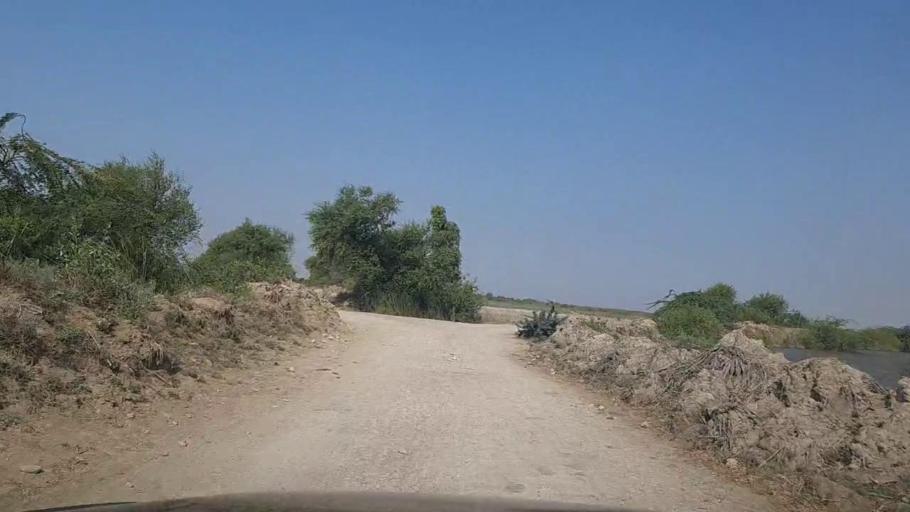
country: PK
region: Sindh
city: Thatta
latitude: 24.6372
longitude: 67.8136
